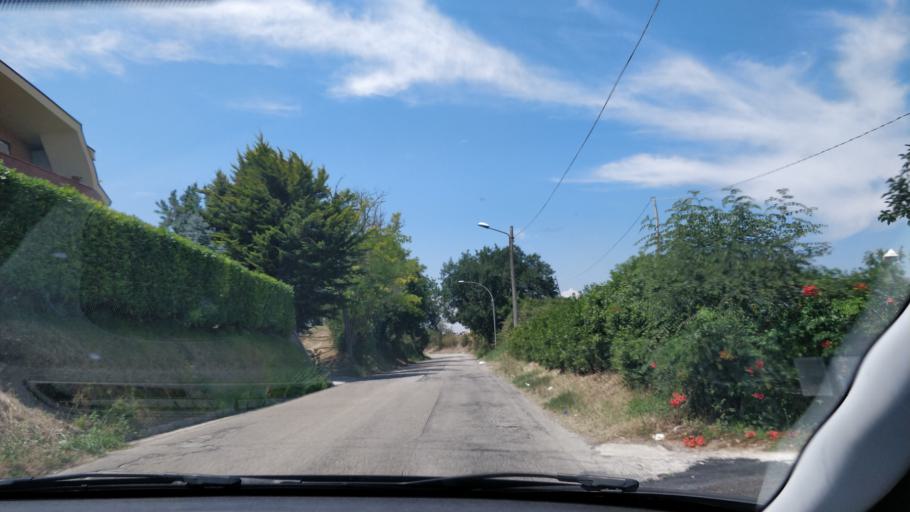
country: IT
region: Abruzzo
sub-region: Provincia di Chieti
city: Francavilla al Mare
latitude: 42.4238
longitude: 14.2590
